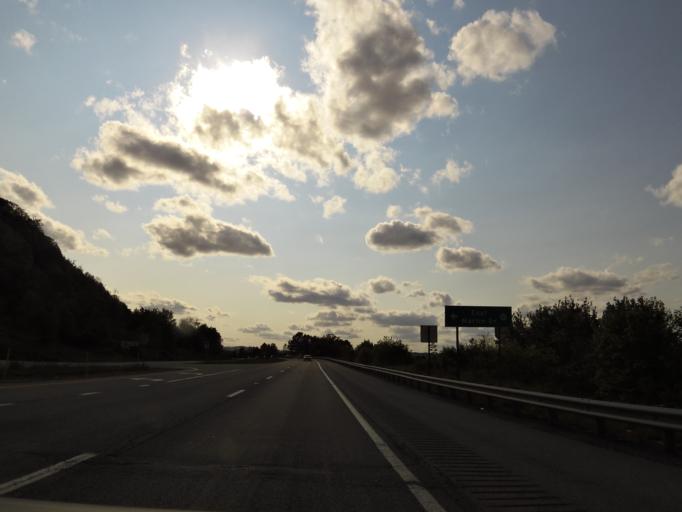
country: US
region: West Virginia
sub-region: Mercer County
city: Princeton
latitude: 37.3623
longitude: -81.0682
